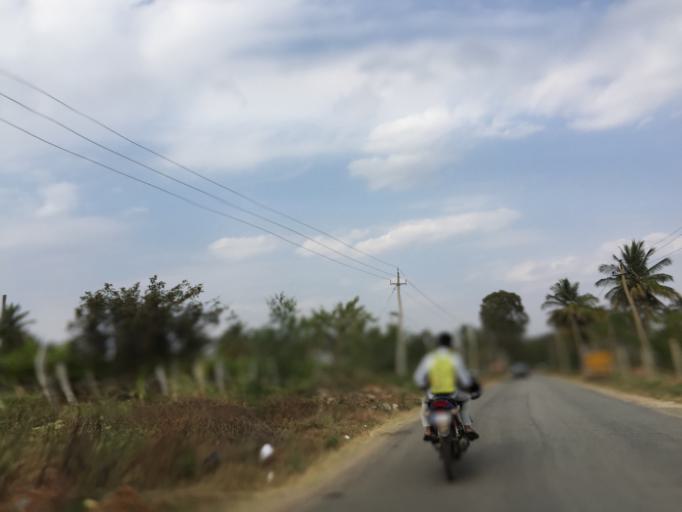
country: IN
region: Karnataka
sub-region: Chikkaballapur
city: Chik Ballapur
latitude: 13.3933
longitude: 77.7012
